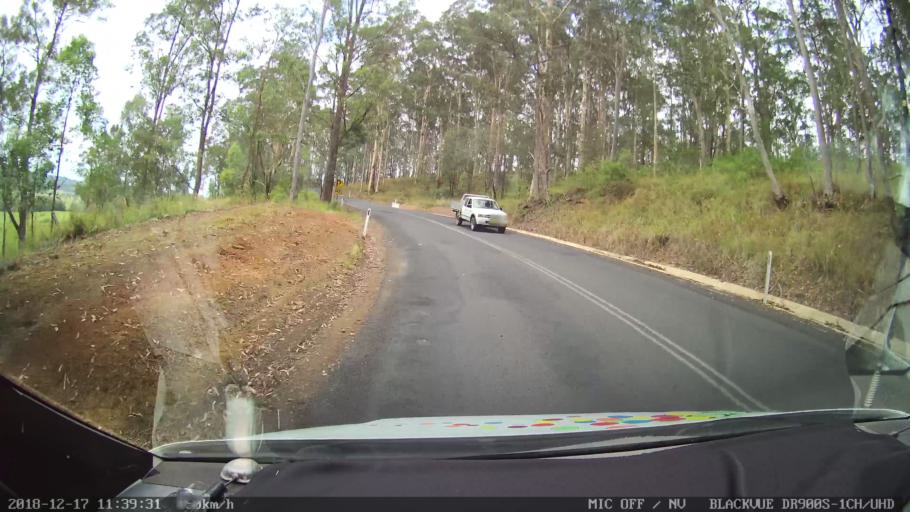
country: AU
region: New South Wales
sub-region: Kyogle
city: Kyogle
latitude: -28.6871
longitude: 152.5940
